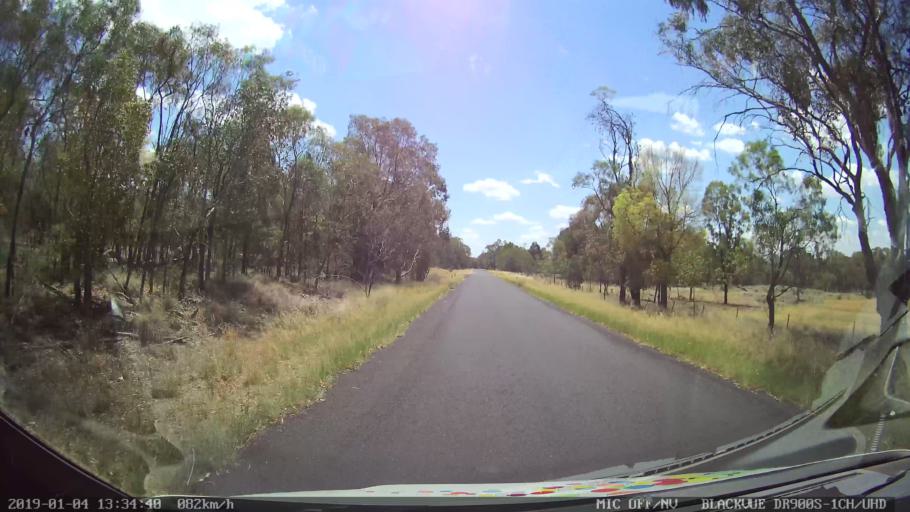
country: AU
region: New South Wales
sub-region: Dubbo Municipality
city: Dubbo
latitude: -32.5826
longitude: 148.5365
